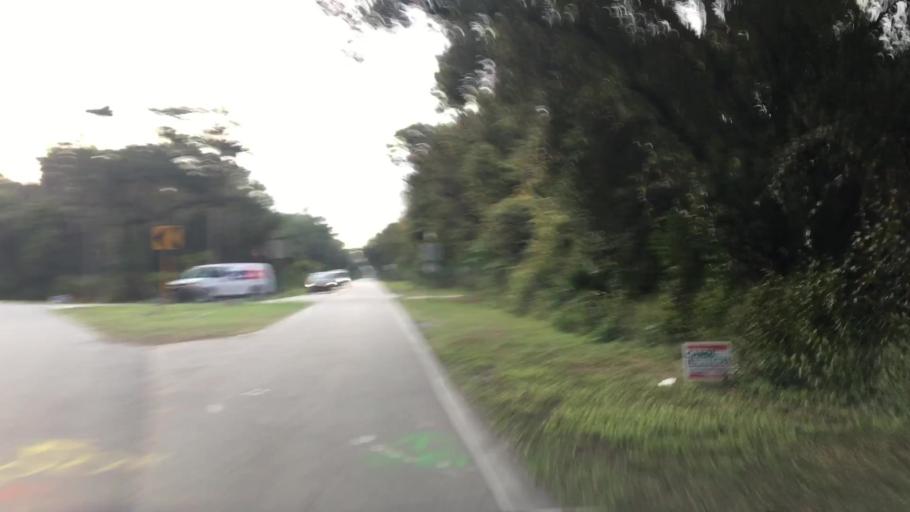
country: US
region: Florida
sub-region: Seminole County
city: Midway
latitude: 28.8477
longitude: -81.2024
